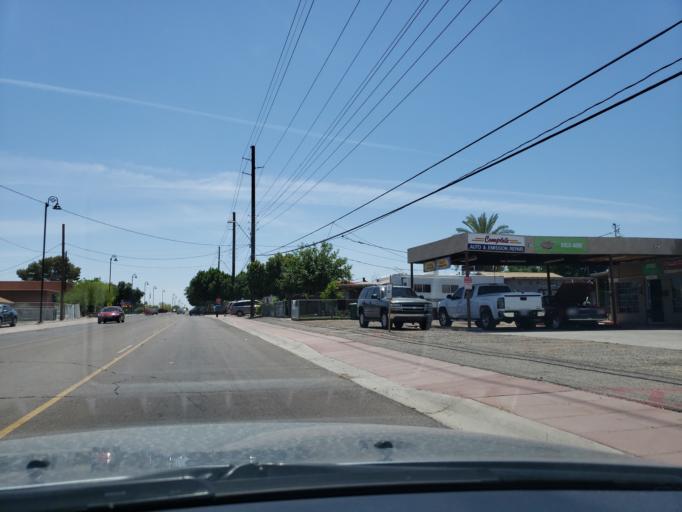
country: US
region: Arizona
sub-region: Maricopa County
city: Guadalupe
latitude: 33.3719
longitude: -111.9632
